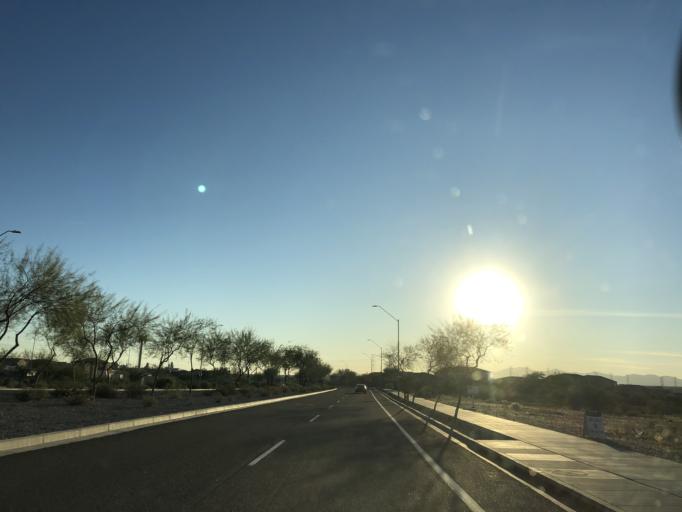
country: US
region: Arizona
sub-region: Maricopa County
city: Sun City West
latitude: 33.7112
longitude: -112.2865
